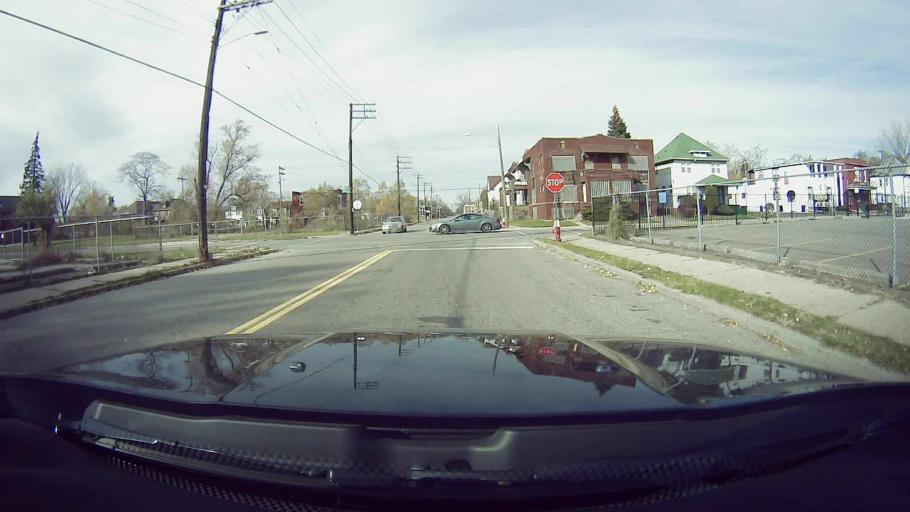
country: US
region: Michigan
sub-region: Wayne County
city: Hamtramck
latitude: 42.3847
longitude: -83.0754
